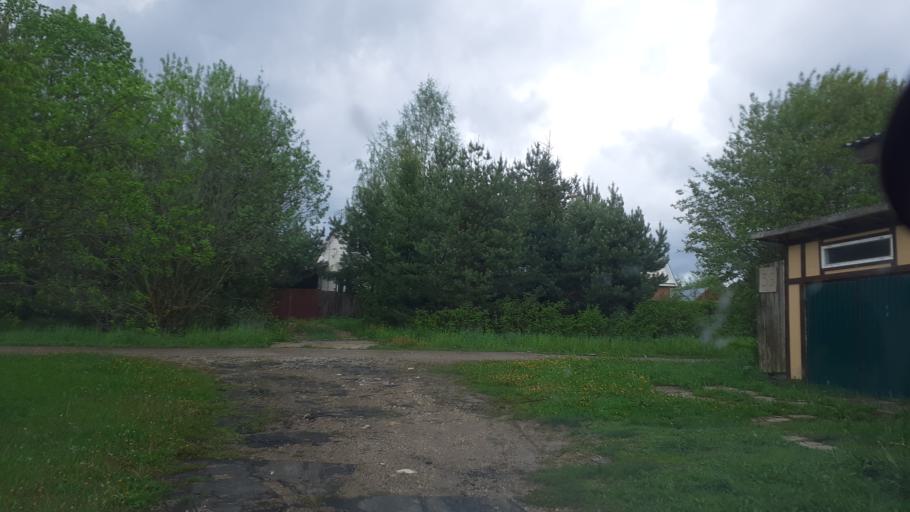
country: RU
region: Moskovskaya
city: Sychevo
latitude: 55.9624
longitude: 36.2695
